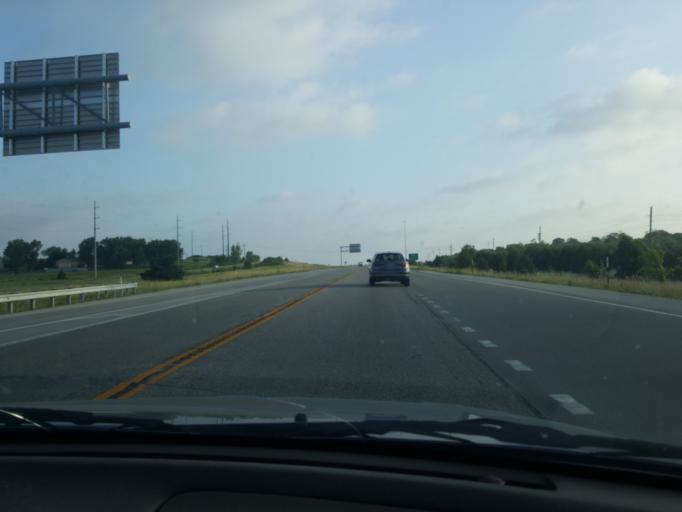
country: US
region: Kansas
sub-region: Douglas County
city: Lawrence
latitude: 38.9637
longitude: -95.3341
